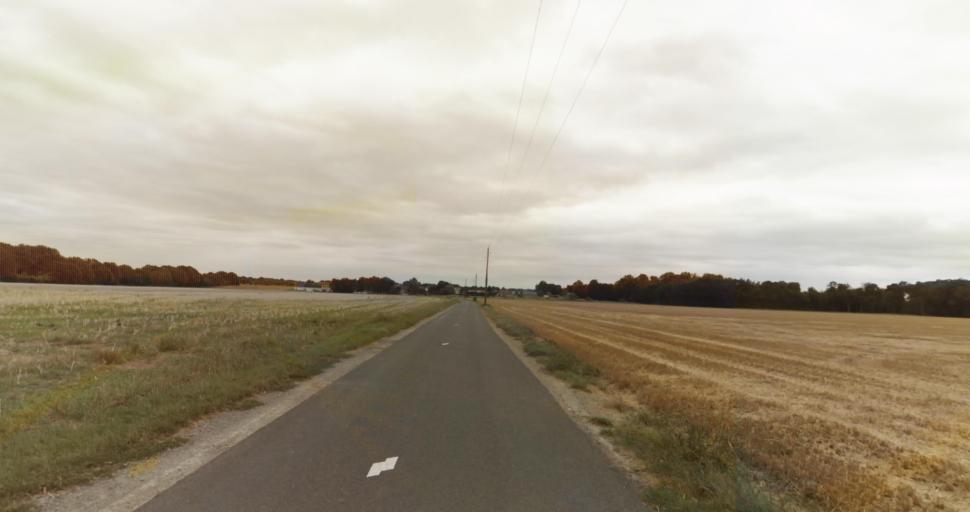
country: FR
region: Haute-Normandie
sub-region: Departement de l'Eure
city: Evreux
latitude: 48.9966
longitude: 1.2100
